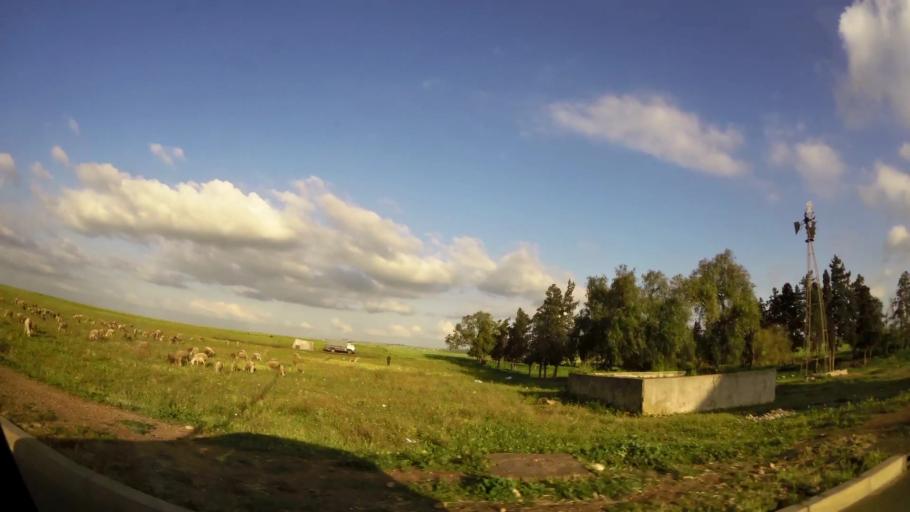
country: MA
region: Chaouia-Ouardigha
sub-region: Settat Province
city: Settat
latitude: 33.0022
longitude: -7.5965
